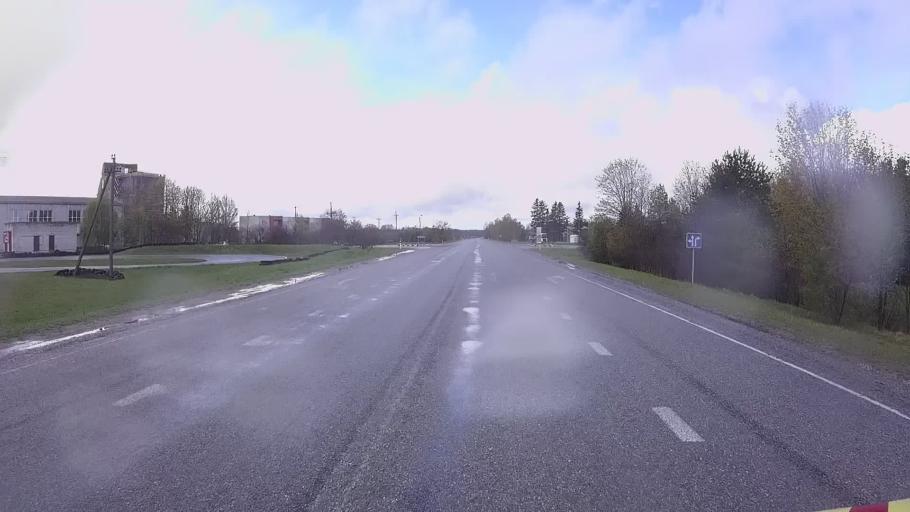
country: EE
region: Hiiumaa
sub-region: Kaerdla linn
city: Kardla
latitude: 58.8320
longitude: 22.7738
